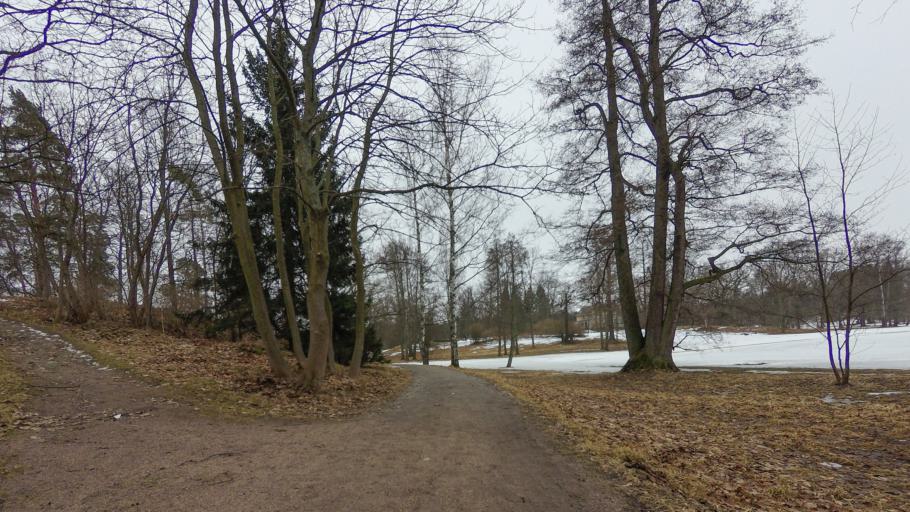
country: FI
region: Uusimaa
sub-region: Helsinki
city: Helsinki
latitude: 60.1802
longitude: 25.0311
